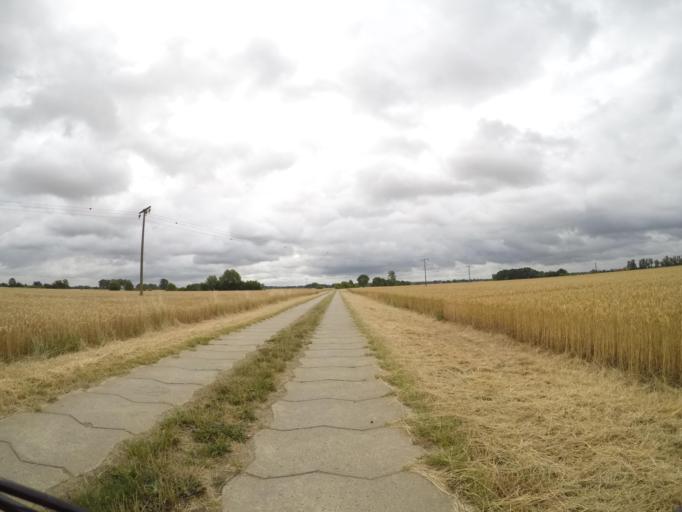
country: DE
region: Lower Saxony
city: Damnatz
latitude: 53.1811
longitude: 11.1166
